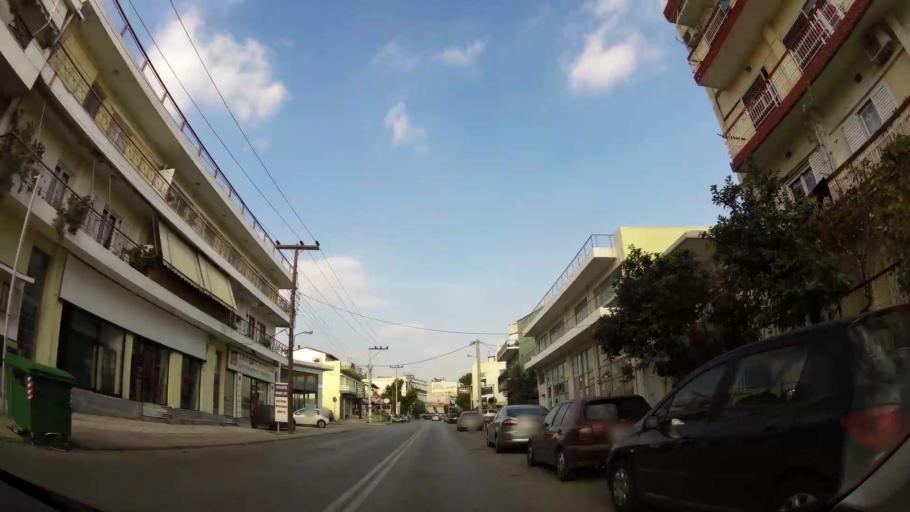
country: GR
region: Attica
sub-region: Nomarchia Anatolikis Attikis
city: Acharnes
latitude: 38.0888
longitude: 23.7322
